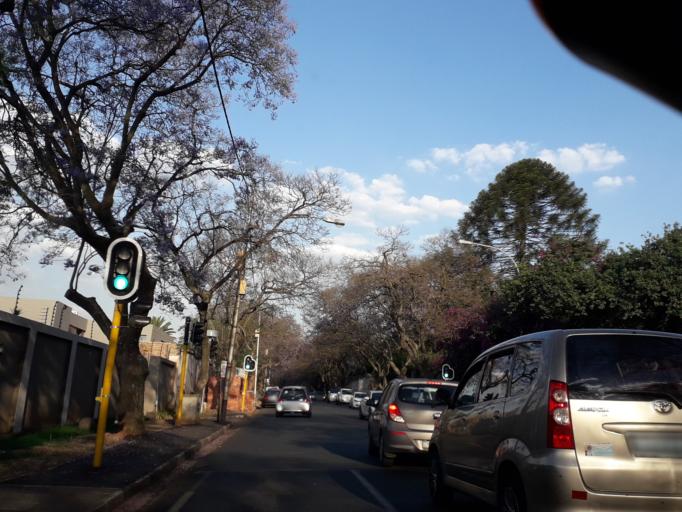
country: ZA
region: Gauteng
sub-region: City of Johannesburg Metropolitan Municipality
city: Johannesburg
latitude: -26.1702
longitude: 28.0631
